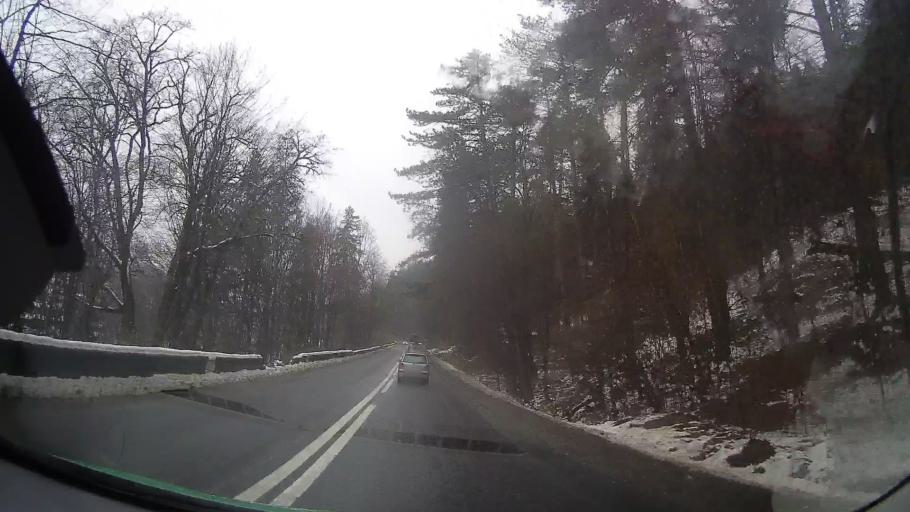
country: RO
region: Neamt
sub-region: Comuna Tarcau
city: Tarcau
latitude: 46.8959
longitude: 26.1227
